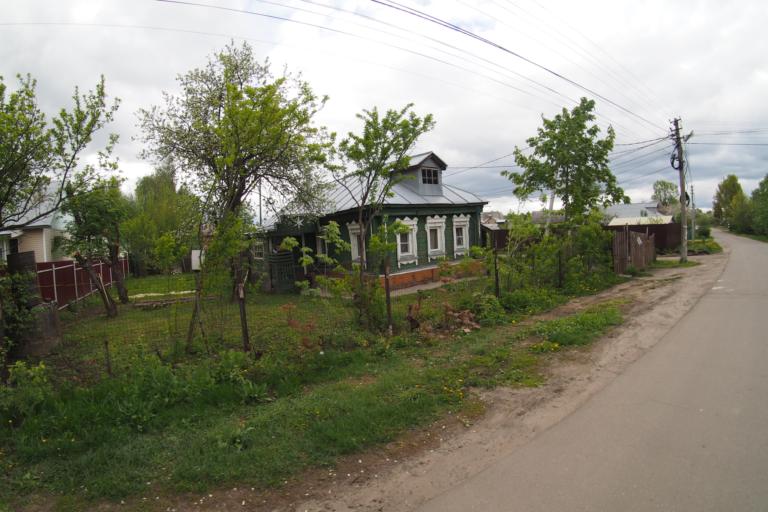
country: RU
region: Moskovskaya
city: Rechitsy
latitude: 55.5801
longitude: 38.5042
